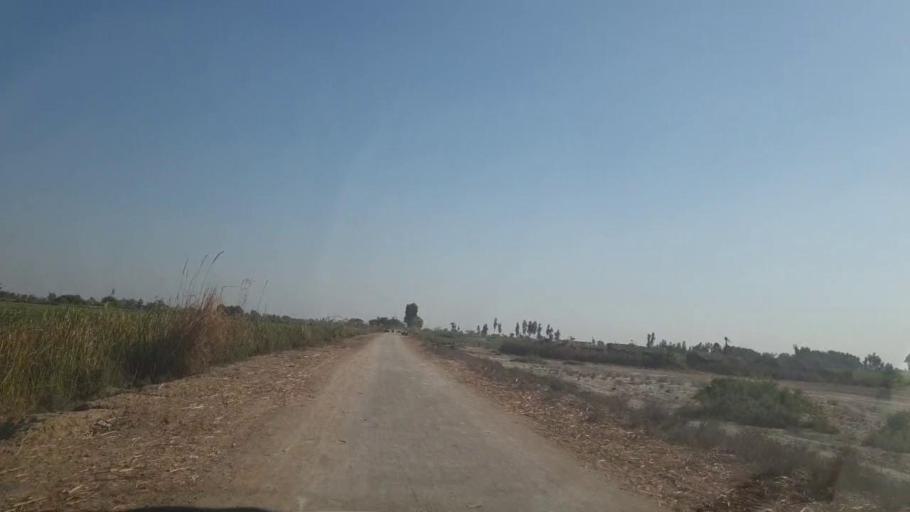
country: PK
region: Sindh
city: Mirpur Khas
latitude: 25.4447
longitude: 69.1435
